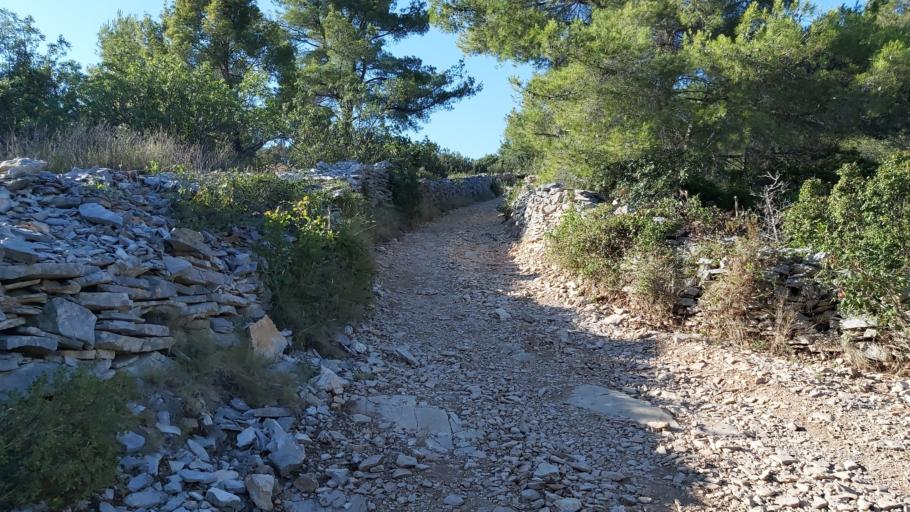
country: HR
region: Splitsko-Dalmatinska
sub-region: Grad Trogir
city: Trogir
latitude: 43.3736
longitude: 16.2868
